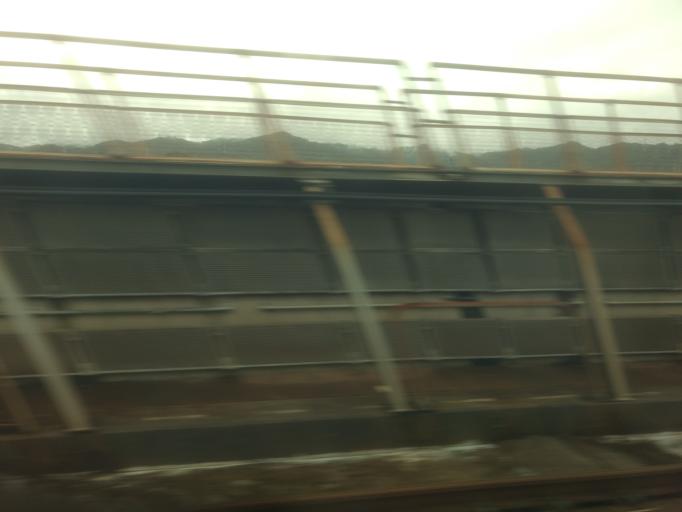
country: JP
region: Yamaguchi
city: Tokuyama
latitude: 34.0337
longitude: 131.8406
